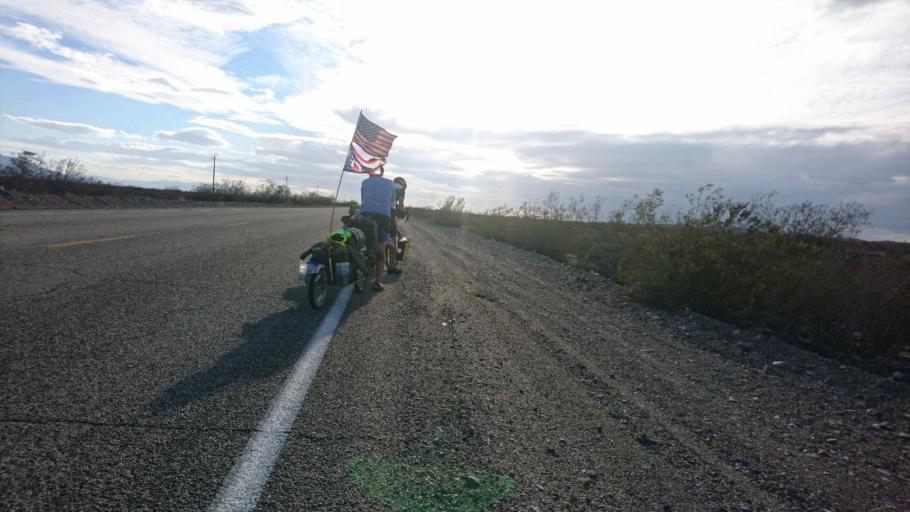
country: US
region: California
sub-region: San Bernardino County
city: Needles
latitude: 34.6744
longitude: -115.3346
